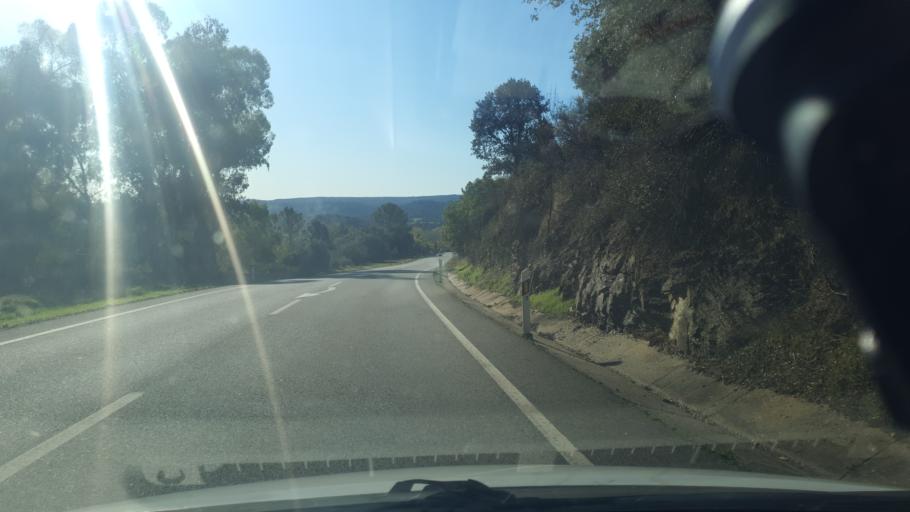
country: ES
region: Castille and Leon
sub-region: Provincia de Avila
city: Arenas de San Pedro
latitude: 40.1908
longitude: -5.0465
